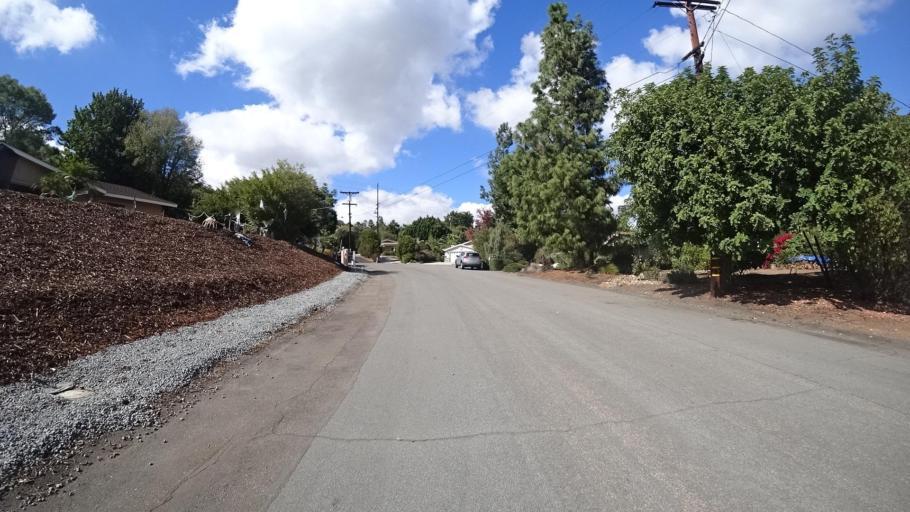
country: US
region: California
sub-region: San Diego County
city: Casa de Oro-Mount Helix
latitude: 32.7609
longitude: -116.9524
